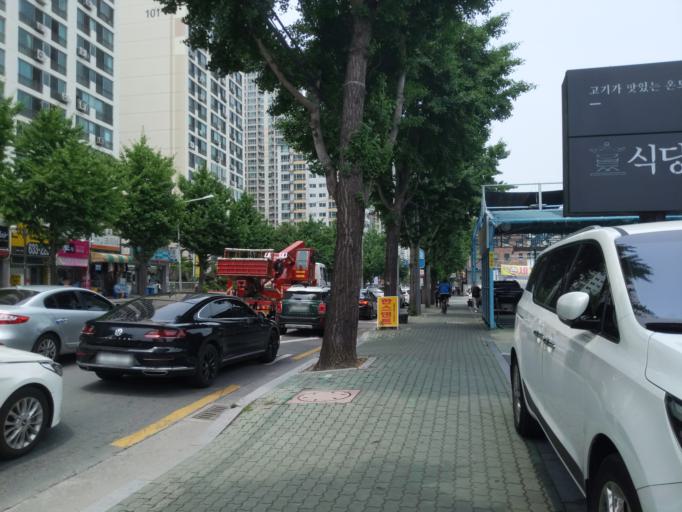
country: KR
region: Daegu
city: Hwawon
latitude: 35.8118
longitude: 128.5254
